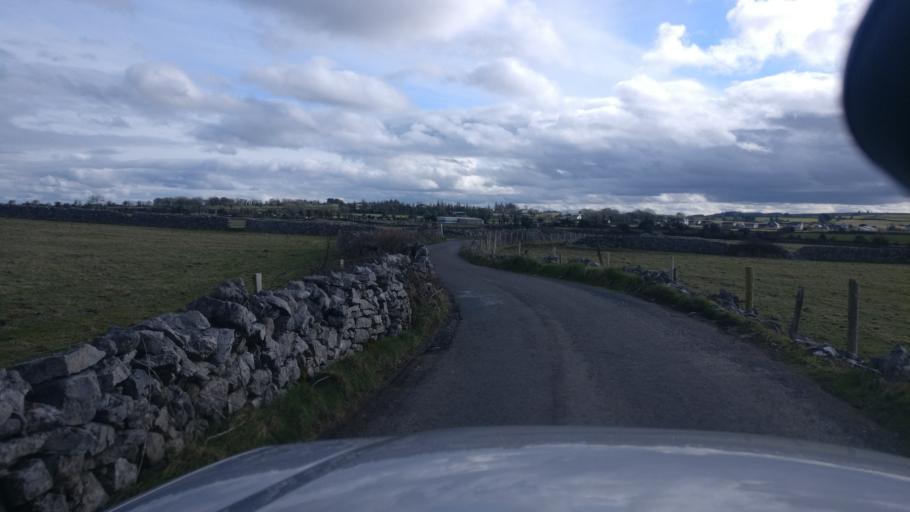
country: IE
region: Connaught
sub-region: County Galway
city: Loughrea
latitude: 53.2000
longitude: -8.5428
